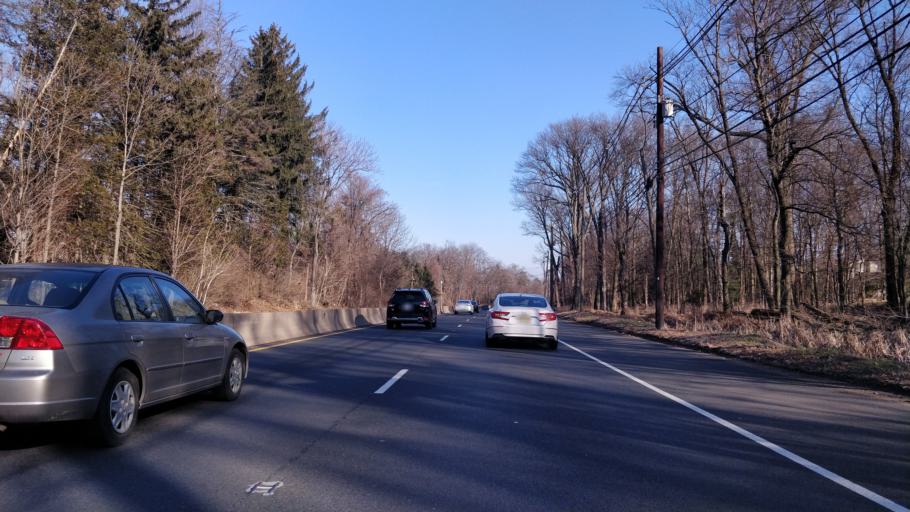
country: US
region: New Jersey
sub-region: Union County
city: Scotch Plains
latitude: 40.6683
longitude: -74.3761
